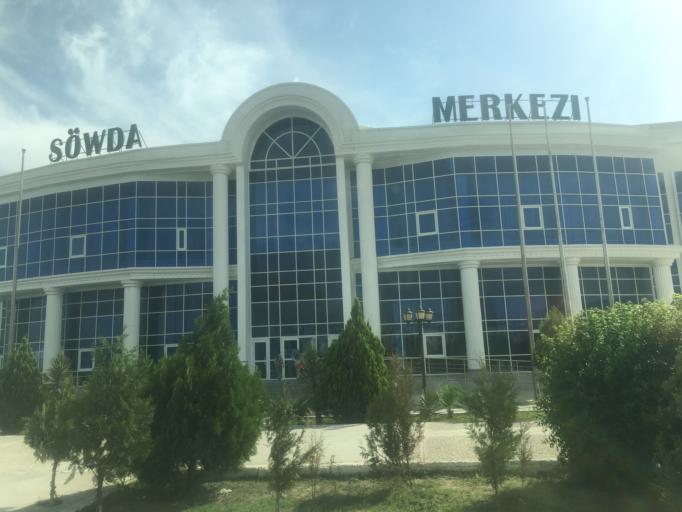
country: TM
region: Balkan
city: Balkanabat
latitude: 39.5194
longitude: 54.3384
